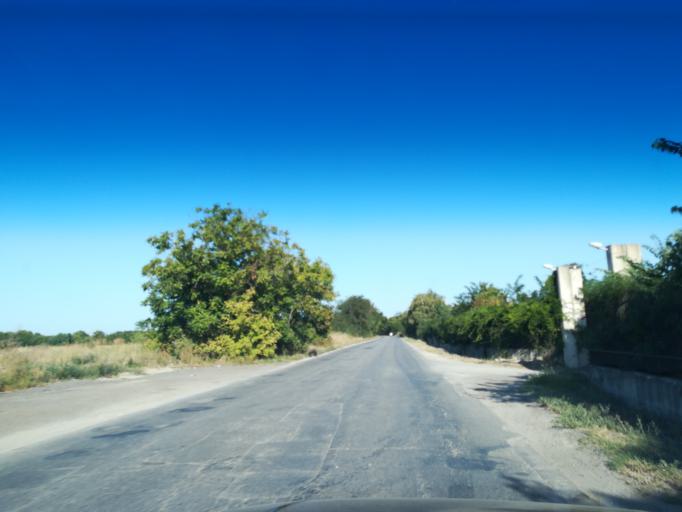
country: BG
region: Plovdiv
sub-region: Obshtina Plovdiv
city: Plovdiv
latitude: 42.1656
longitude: 24.8011
